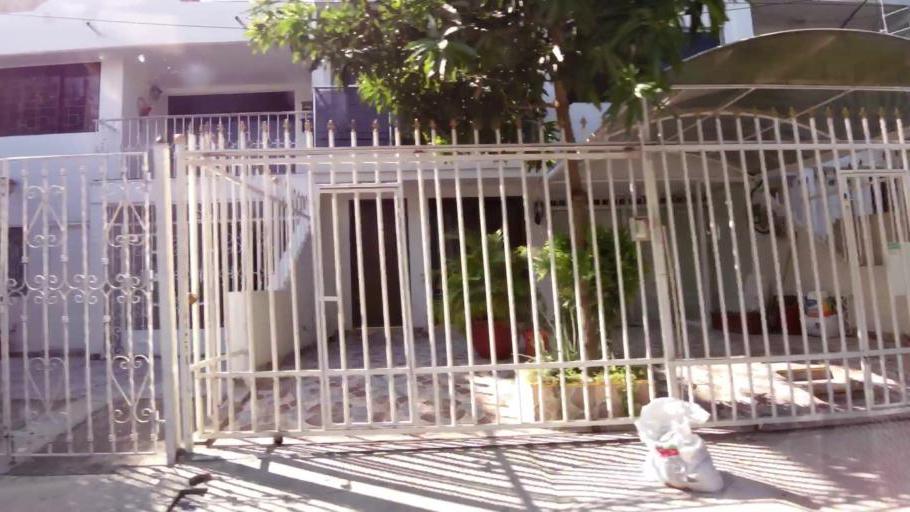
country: CO
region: Bolivar
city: Cartagena
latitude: 10.3830
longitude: -75.4753
